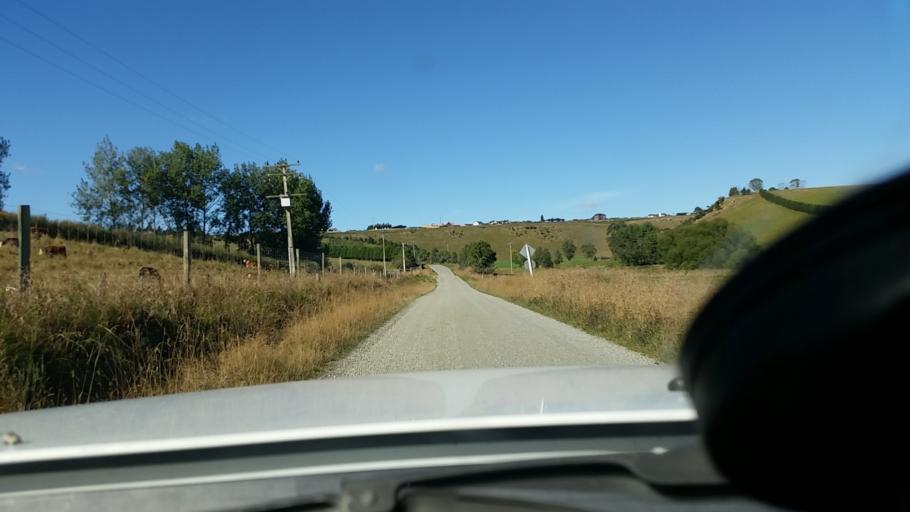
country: NZ
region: Canterbury
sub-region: Timaru District
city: Pleasant Point
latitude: -44.3462
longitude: 171.1579
